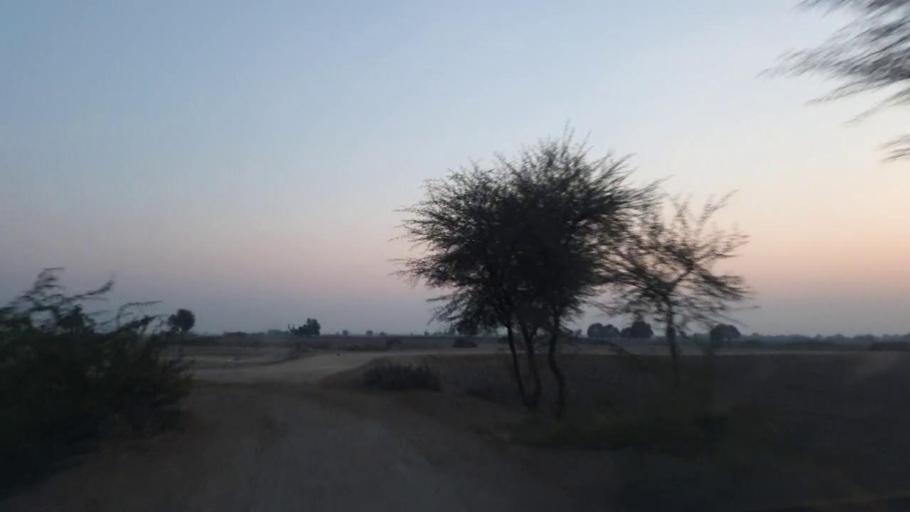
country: PK
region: Sindh
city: Naukot
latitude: 25.0183
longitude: 69.4117
